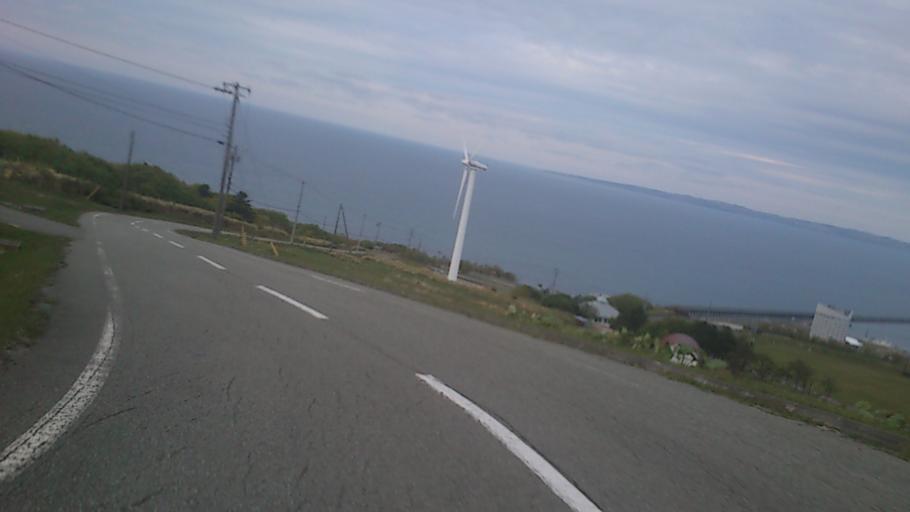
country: JP
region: Hokkaido
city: Wakkanai
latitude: 45.4172
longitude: 141.6660
